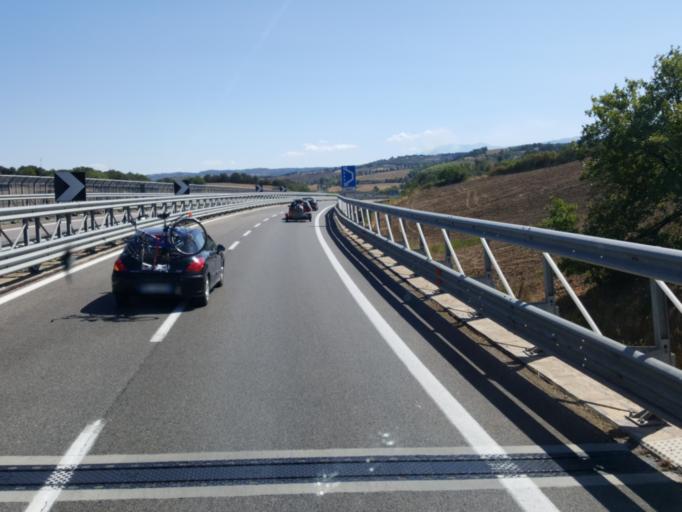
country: IT
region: Tuscany
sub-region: Provincia di Grosseto
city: Campagnatico
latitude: 42.8866
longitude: 11.2245
